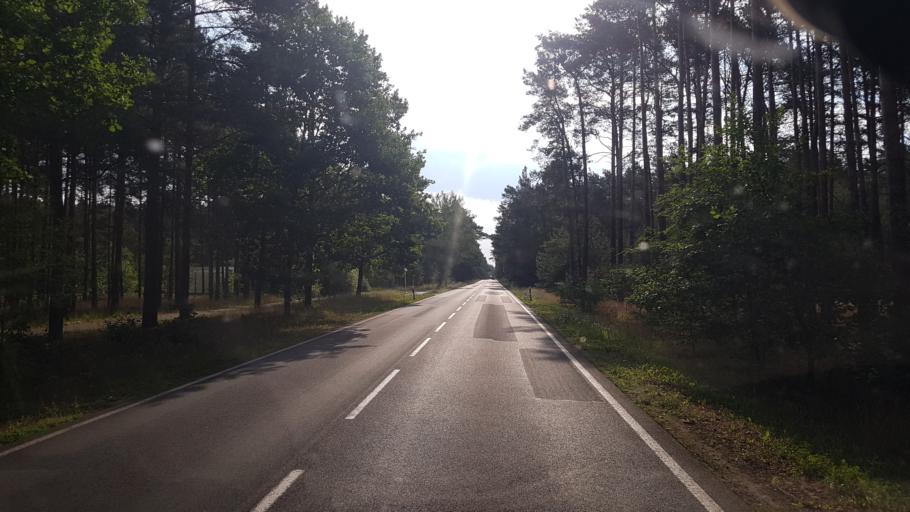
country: DE
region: Brandenburg
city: Baruth
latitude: 52.0576
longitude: 13.5342
